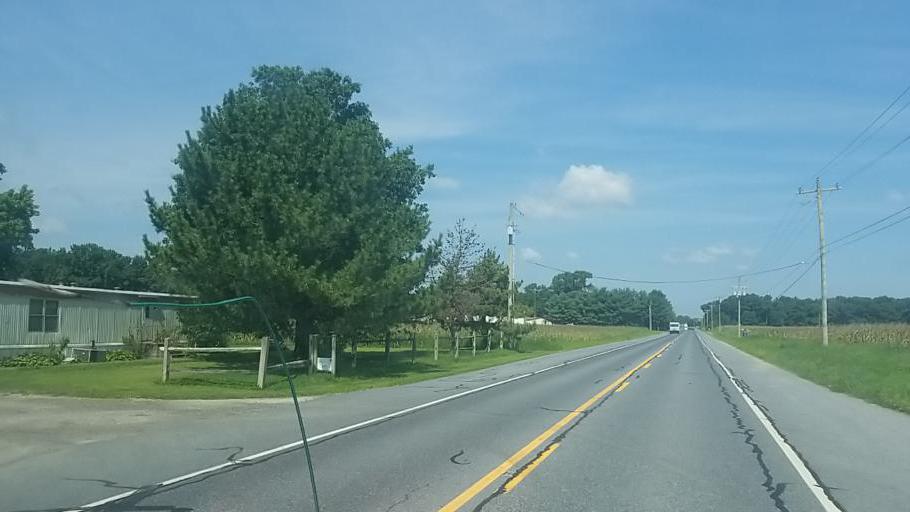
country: US
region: Delaware
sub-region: Sussex County
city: Seaford
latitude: 38.6773
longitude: -75.5795
